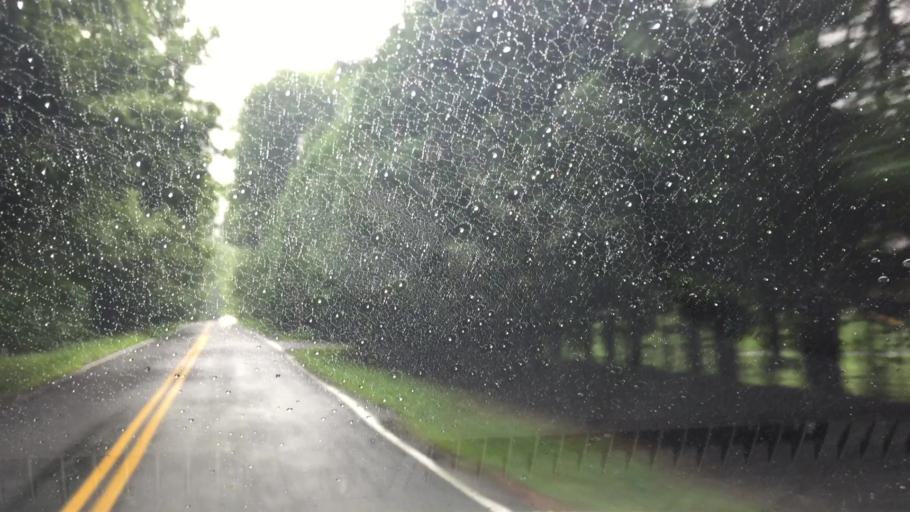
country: US
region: Massachusetts
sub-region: Berkshire County
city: West Stockbridge
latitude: 42.3024
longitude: -73.3784
